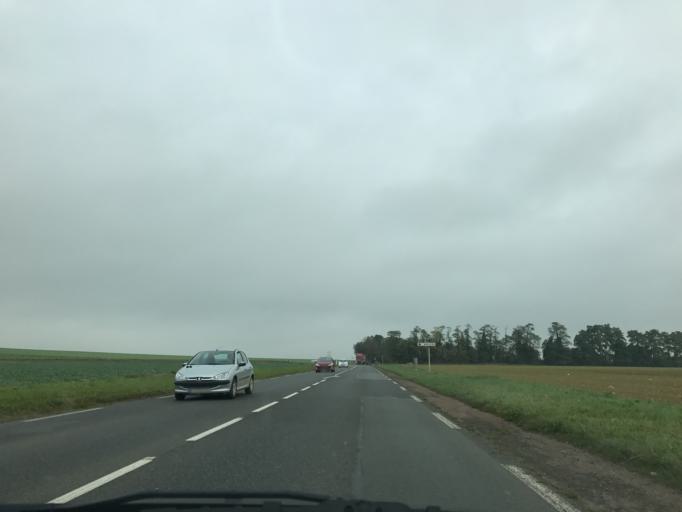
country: FR
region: Picardie
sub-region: Departement de la Somme
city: Peronne
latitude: 49.8976
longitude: 2.9224
